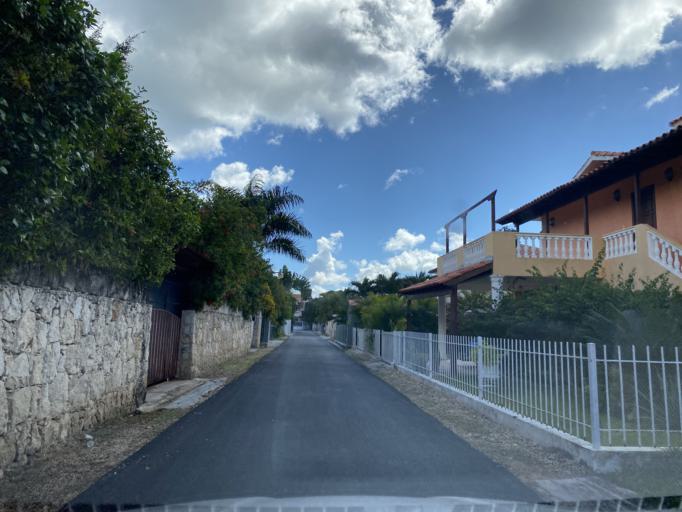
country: DO
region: La Romana
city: La Romana
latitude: 18.3495
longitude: -68.8270
